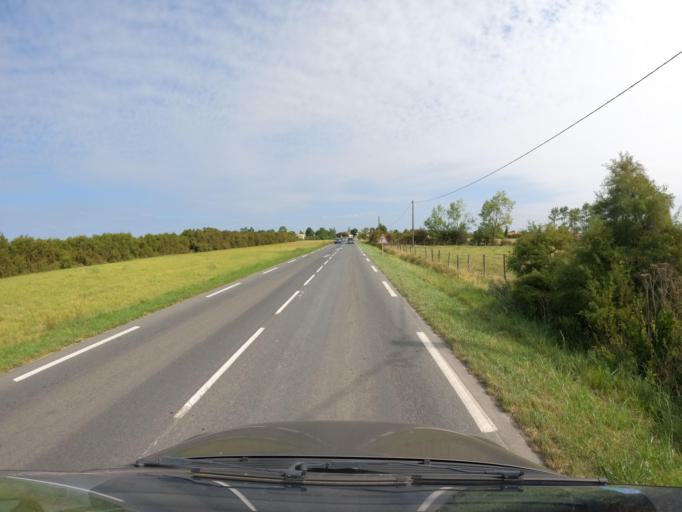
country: FR
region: Pays de la Loire
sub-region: Departement de la Vendee
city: Triaize
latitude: 46.3870
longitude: -1.2018
